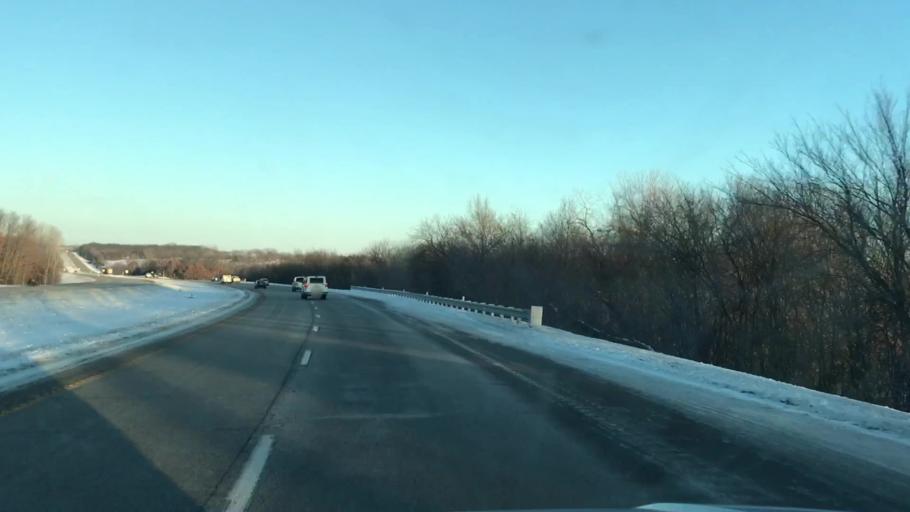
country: US
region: Missouri
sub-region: Clinton County
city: Gower
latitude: 39.7470
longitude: -94.6072
